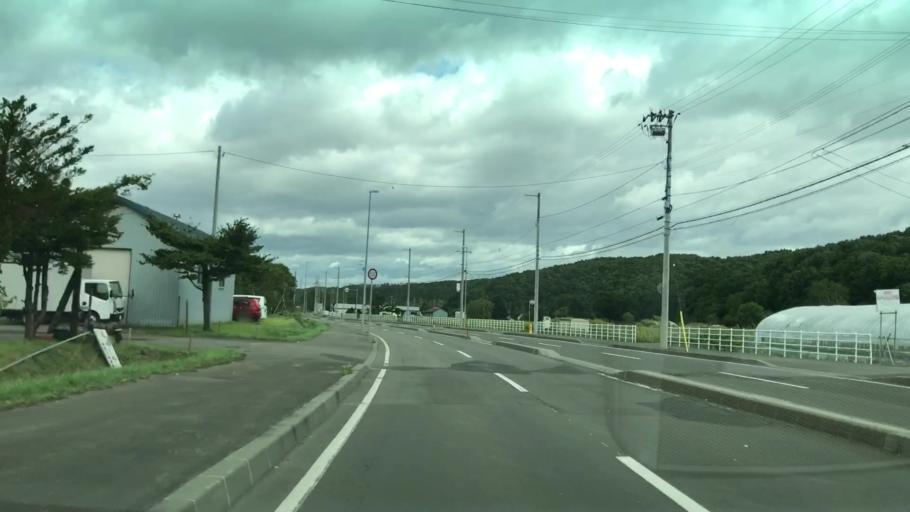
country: JP
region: Hokkaido
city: Kitahiroshima
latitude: 42.9610
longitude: 141.4560
